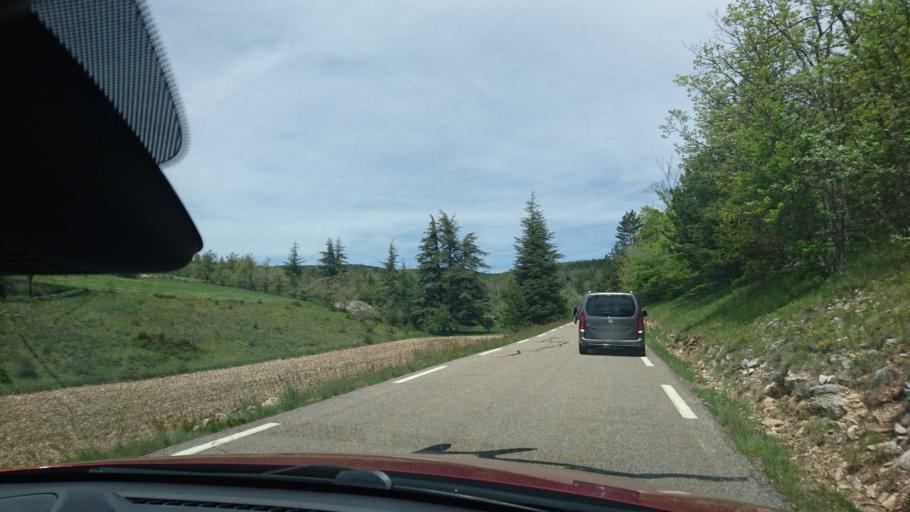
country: FR
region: Provence-Alpes-Cote d'Azur
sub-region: Departement du Vaucluse
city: Sault
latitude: 44.1314
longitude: 5.3737
